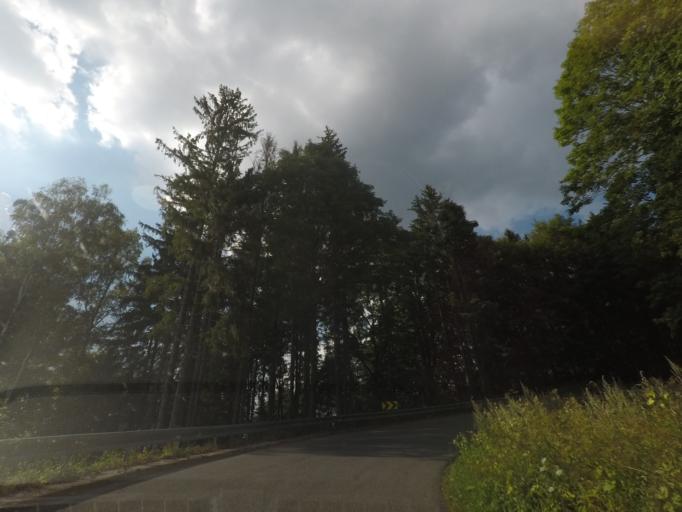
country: CZ
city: Radvanice
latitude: 50.6028
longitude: 16.0495
